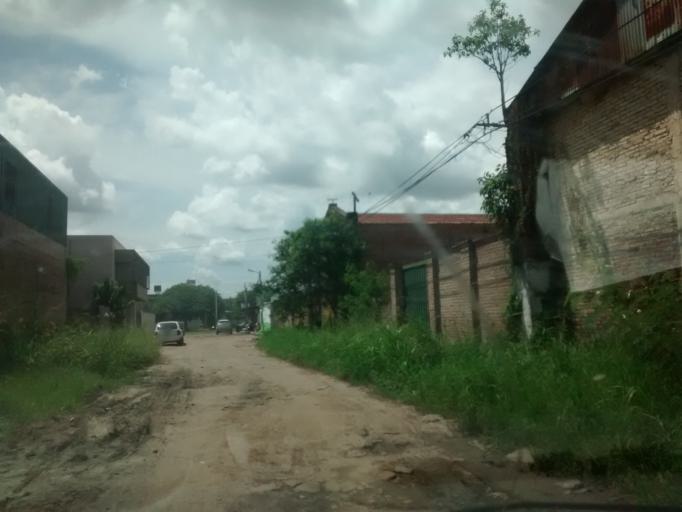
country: AR
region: Chaco
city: Resistencia
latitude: -27.4477
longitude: -58.9984
